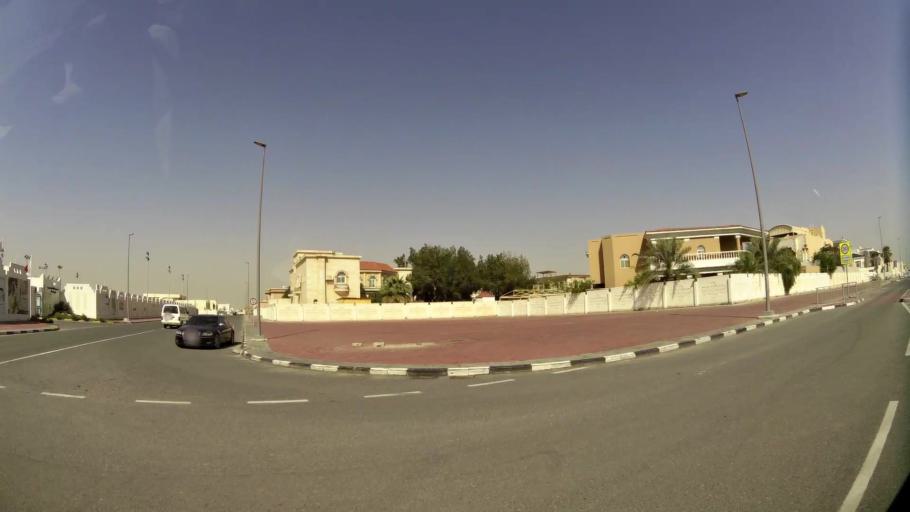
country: QA
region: Baladiyat ad Dawhah
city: Doha
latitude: 25.3577
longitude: 51.5156
